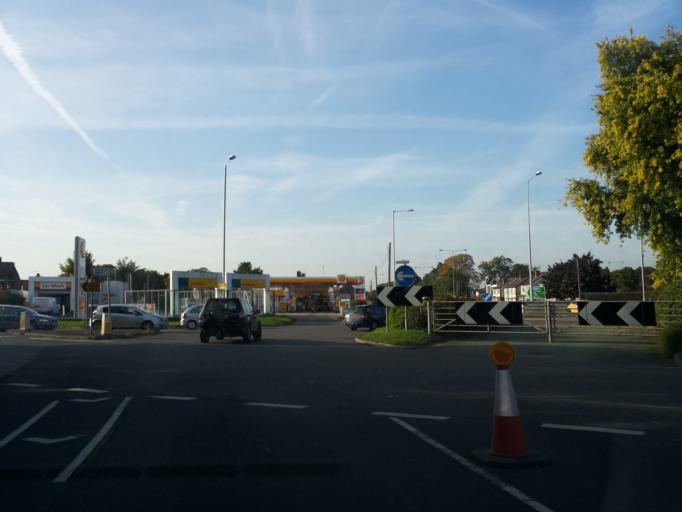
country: GB
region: England
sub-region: Staffordshire
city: Stone
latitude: 52.8964
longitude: -2.1489
